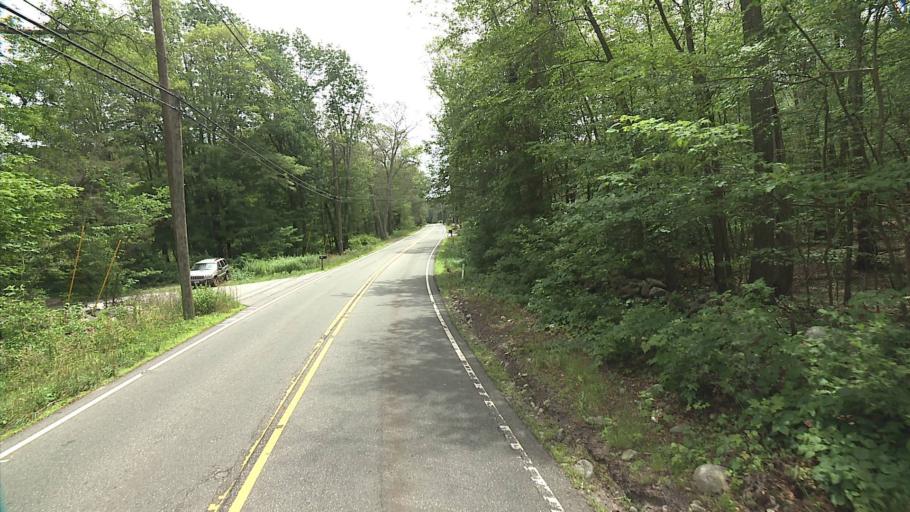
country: US
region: Connecticut
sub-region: New London County
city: Ledyard Center
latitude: 41.4475
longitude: -72.0450
